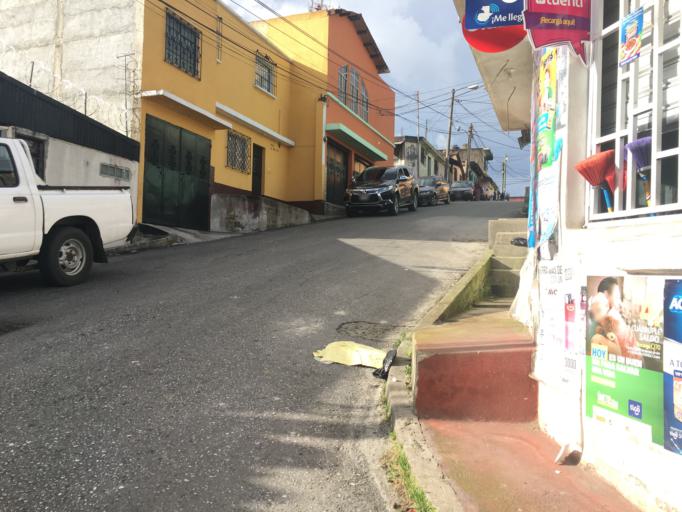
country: GT
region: Guatemala
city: Mixco
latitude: 14.6263
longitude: -90.5834
